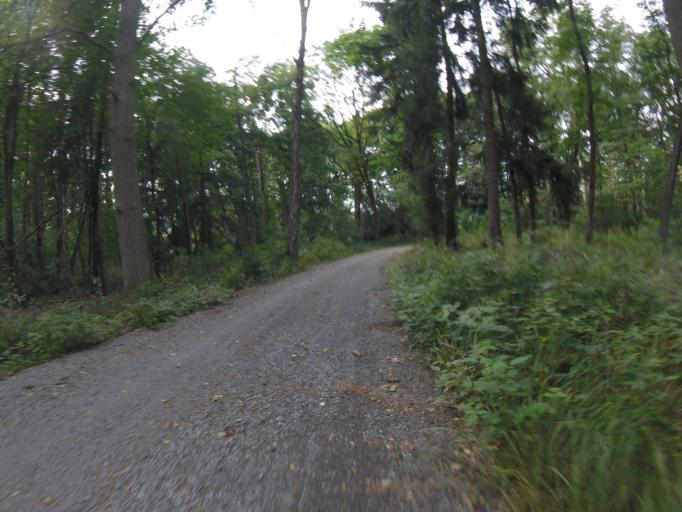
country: DE
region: Brandenburg
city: Halbe
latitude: 52.1523
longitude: 13.7454
